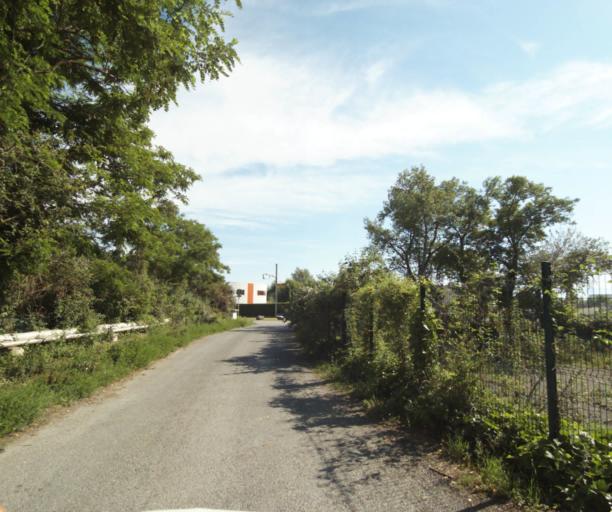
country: FR
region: Rhone-Alpes
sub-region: Departement de la Haute-Savoie
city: Marin
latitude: 46.3886
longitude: 6.5059
